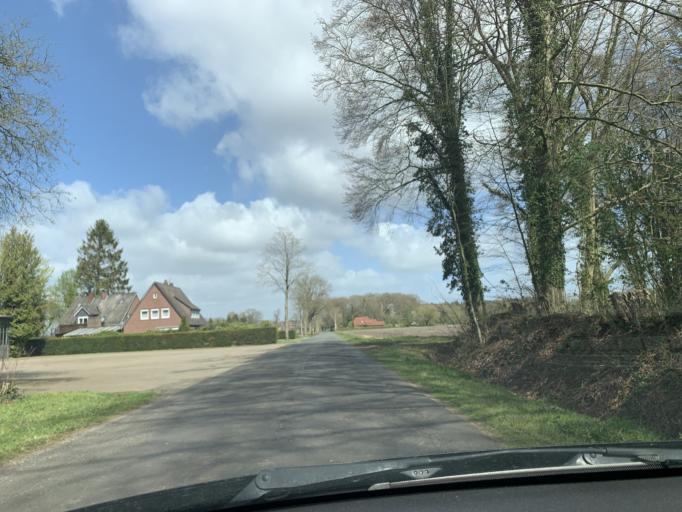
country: DE
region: Lower Saxony
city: Westerstede
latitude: 53.2785
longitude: 7.9421
